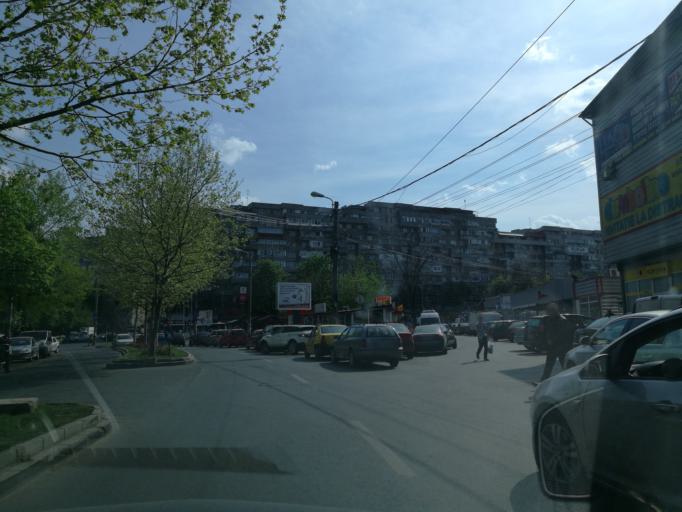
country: RO
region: Ilfov
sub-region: Comuna Chiajna
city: Rosu
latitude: 44.4350
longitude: 26.0207
